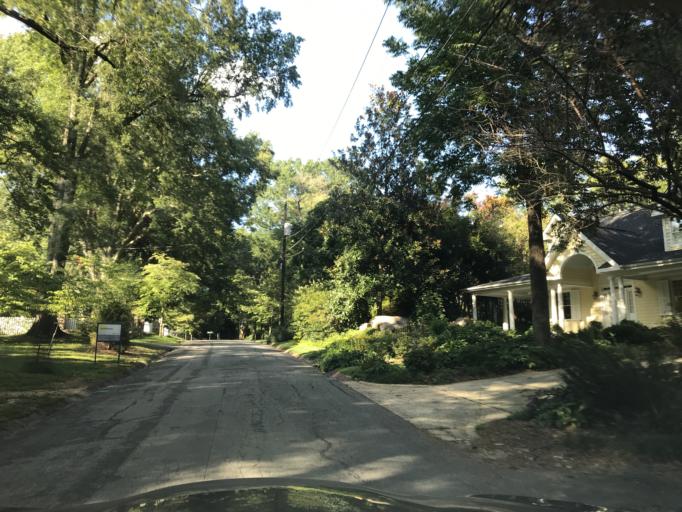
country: US
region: North Carolina
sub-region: Orange County
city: Chapel Hill
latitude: 35.9206
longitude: -79.0450
